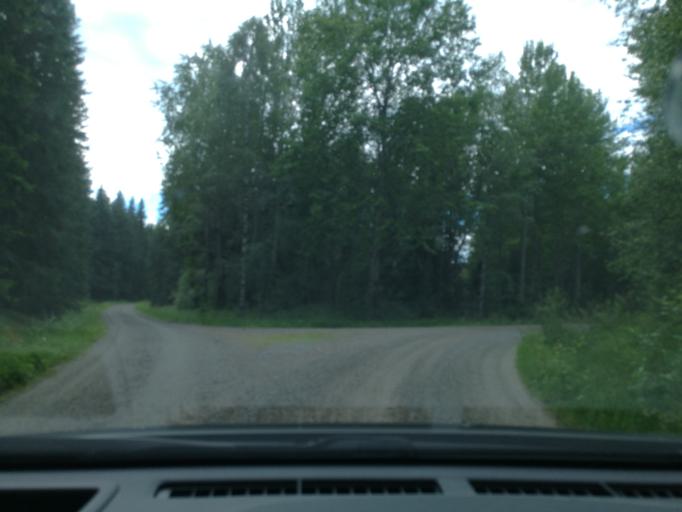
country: SE
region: Vaestmanland
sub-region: Surahammars Kommun
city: Ramnas
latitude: 59.8130
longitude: 16.3126
